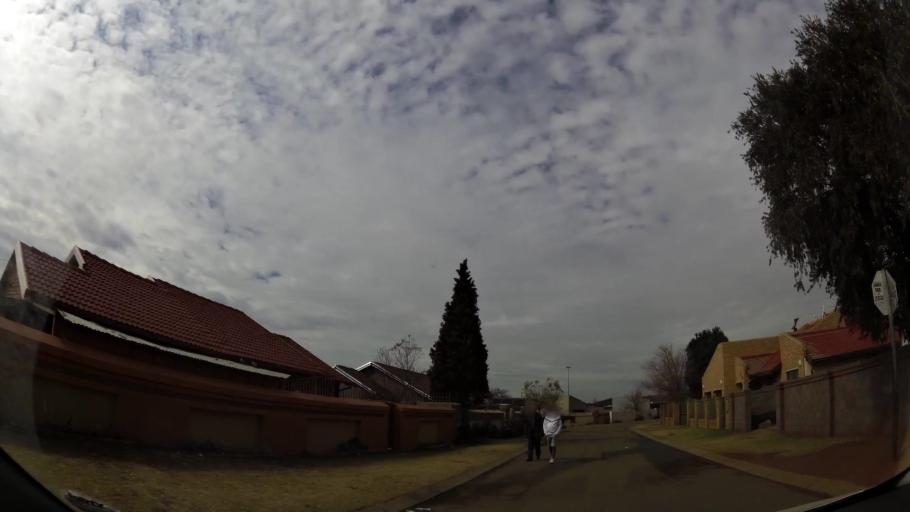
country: ZA
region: Gauteng
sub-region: Ekurhuleni Metropolitan Municipality
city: Germiston
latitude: -26.3728
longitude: 28.1669
